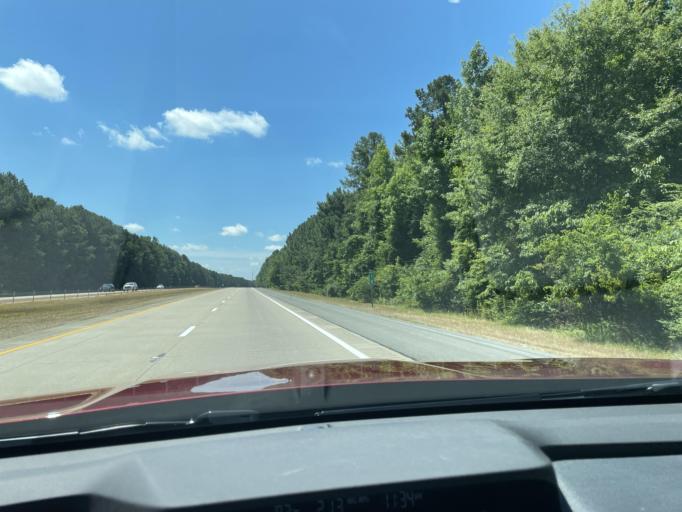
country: US
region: Arkansas
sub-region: Jefferson County
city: Redfield
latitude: 34.4685
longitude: -92.2075
